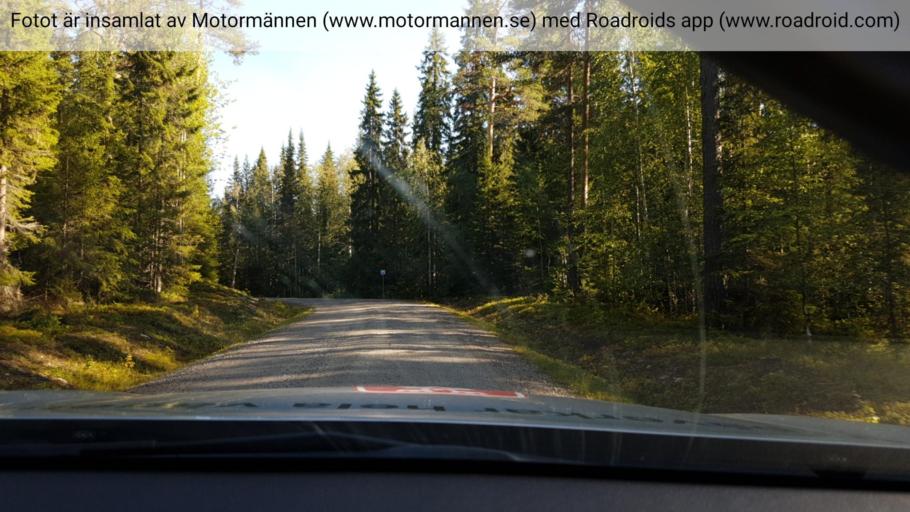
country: SE
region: Vaesterbotten
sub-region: Norsjo Kommun
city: Norsjoe
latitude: 64.7019
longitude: 19.5051
